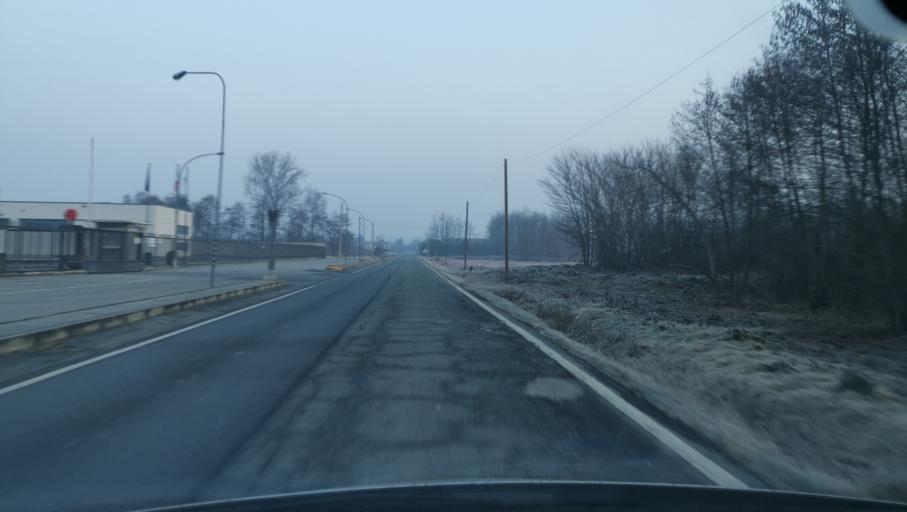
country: IT
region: Piedmont
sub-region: Provincia di Torino
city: San Giusto Canavese
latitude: 45.2995
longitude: 7.8124
